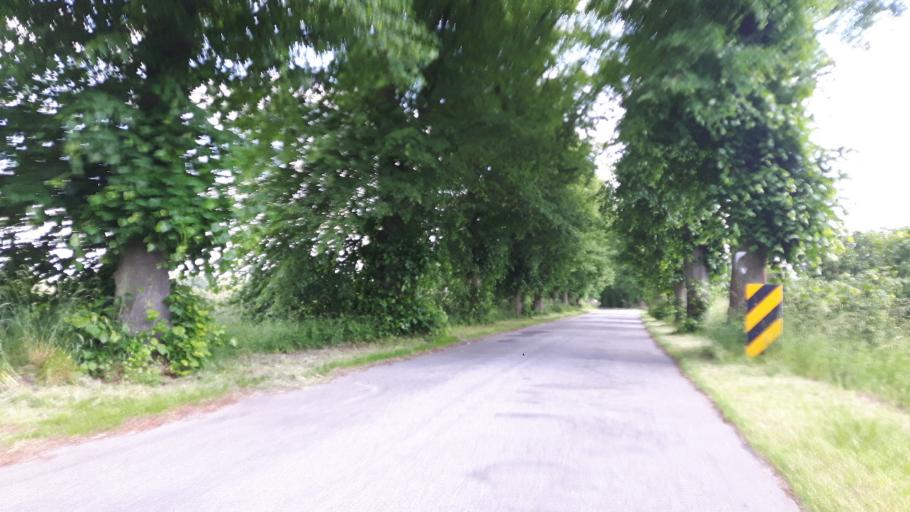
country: PL
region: West Pomeranian Voivodeship
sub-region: Powiat goleniowski
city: Osina
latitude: 53.6794
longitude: 15.0044
